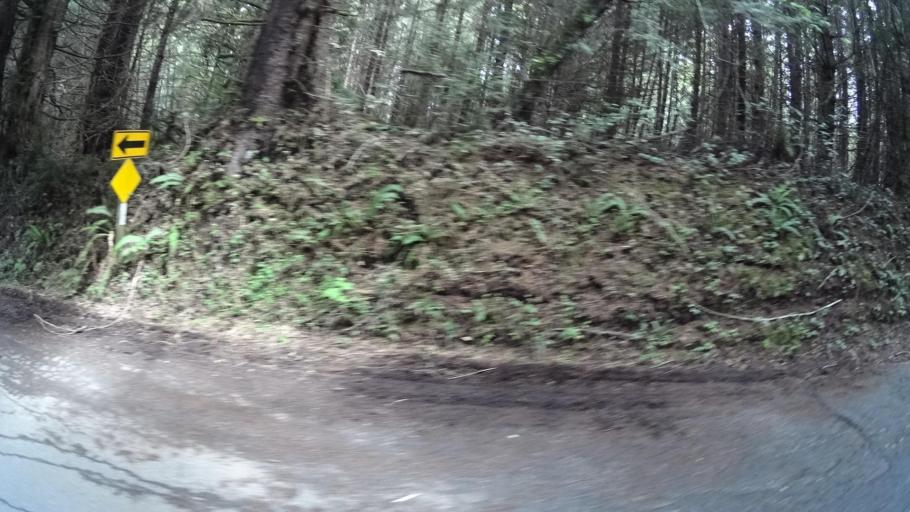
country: US
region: California
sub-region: Humboldt County
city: Bayside
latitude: 40.8346
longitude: -124.0152
